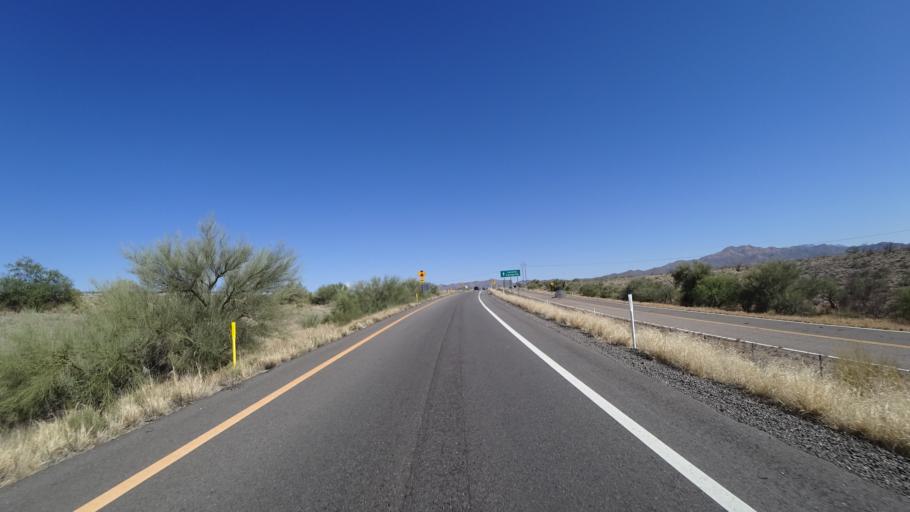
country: US
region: Arizona
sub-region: Pima County
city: Vail
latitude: 32.0065
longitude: -110.6909
